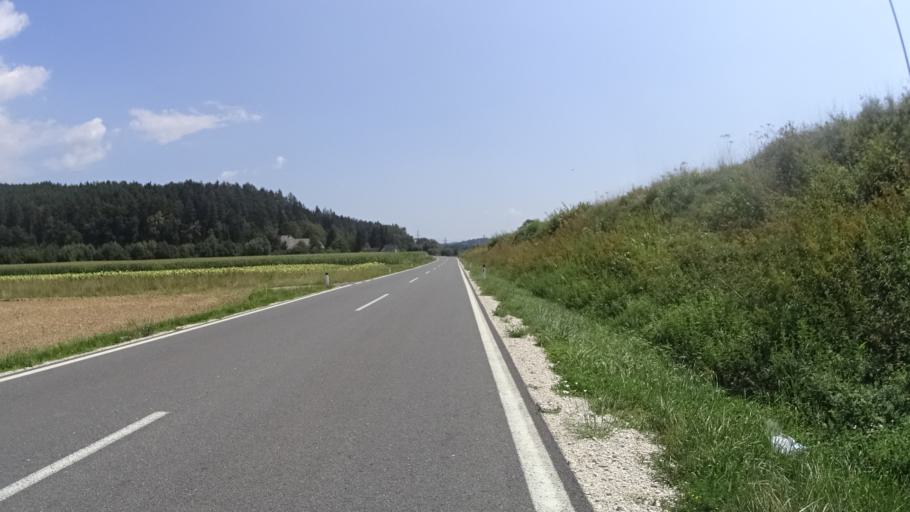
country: AT
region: Carinthia
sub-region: Politischer Bezirk Volkermarkt
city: Bleiburg/Pliberk
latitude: 46.5702
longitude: 14.8092
